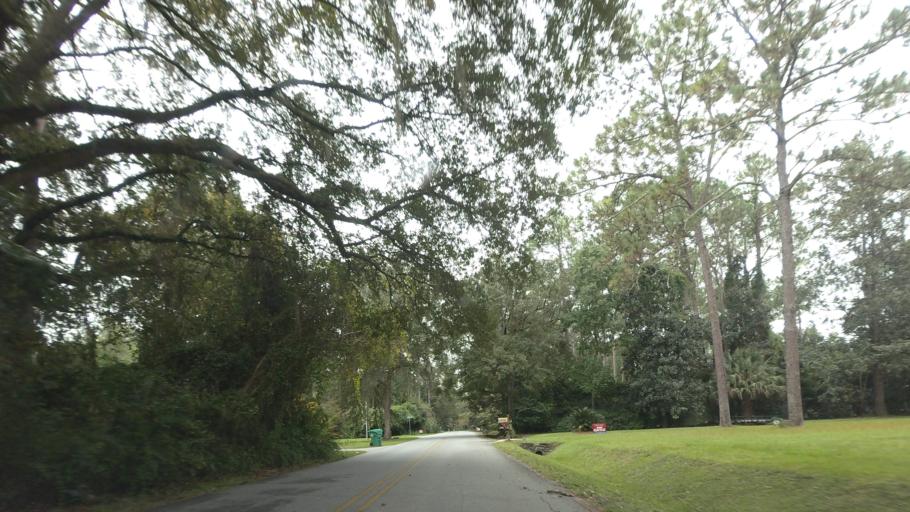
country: US
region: Georgia
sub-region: Lowndes County
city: Remerton
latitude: 30.8588
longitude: -83.2994
